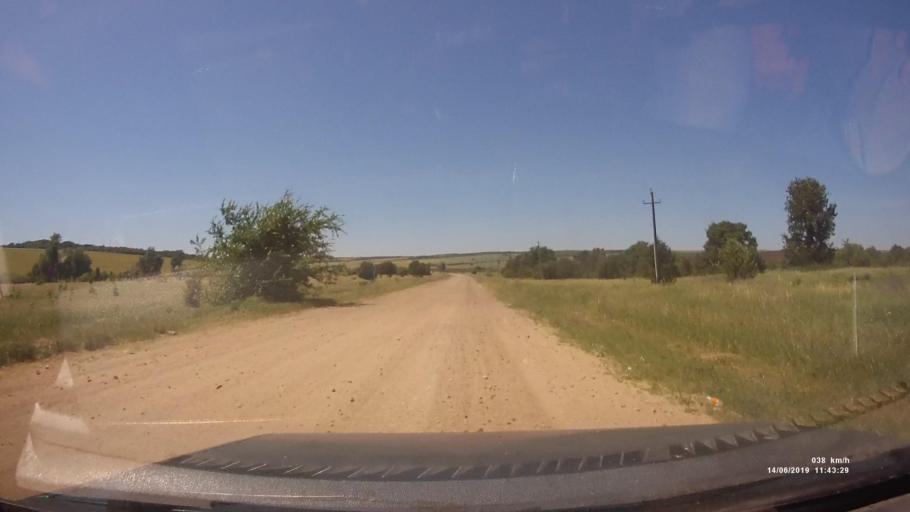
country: RU
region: Rostov
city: Kazanskaya
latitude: 49.8565
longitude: 41.3331
